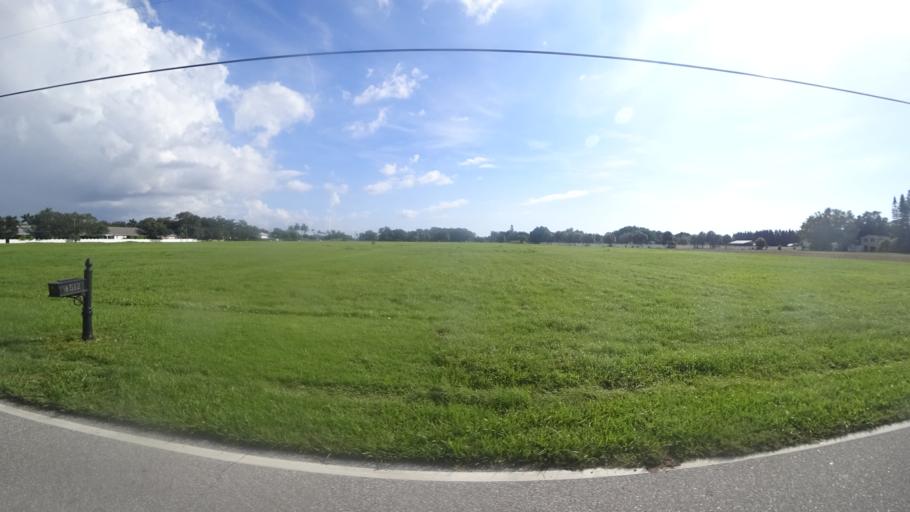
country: US
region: Florida
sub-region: Manatee County
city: West Bradenton
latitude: 27.5299
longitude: -82.6134
